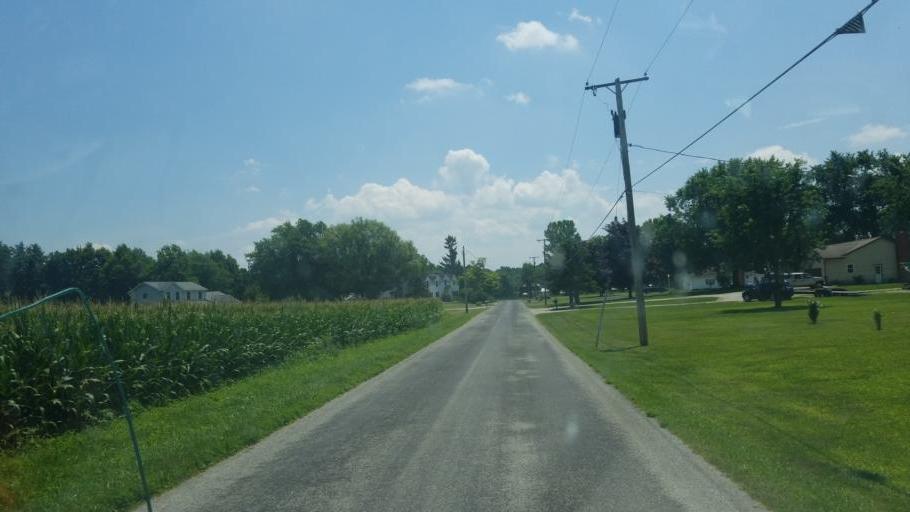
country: US
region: Ohio
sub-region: Richland County
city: Shelby
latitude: 40.8412
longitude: -82.5961
